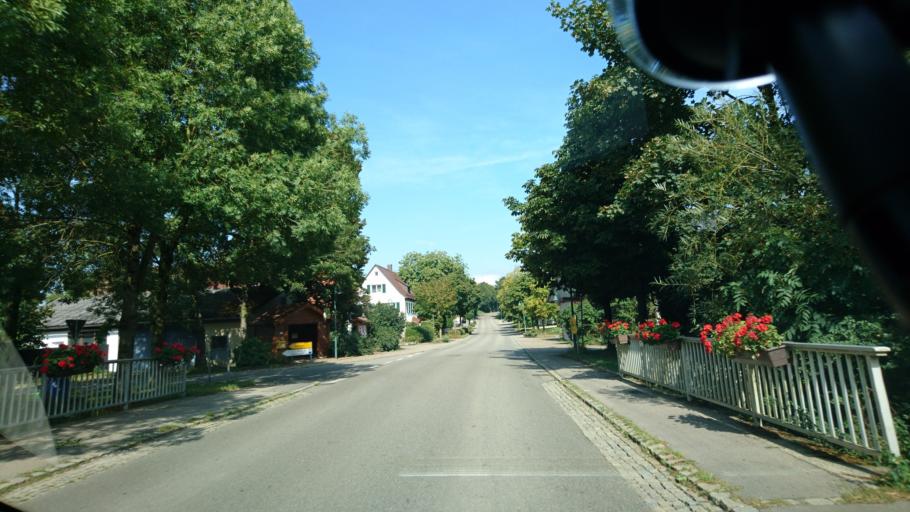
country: DE
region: Baden-Wuerttemberg
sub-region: Regierungsbezirk Stuttgart
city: Wolpertshausen
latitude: 49.1813
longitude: 9.8808
